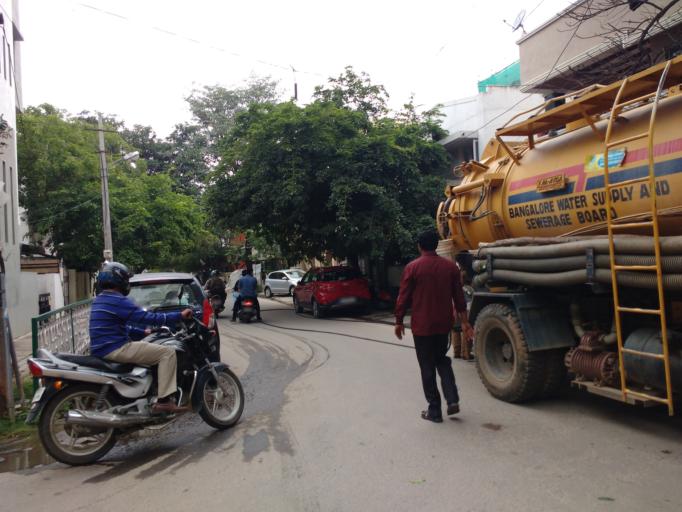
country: IN
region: Karnataka
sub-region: Bangalore Urban
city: Bangalore
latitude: 12.9761
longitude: 77.6357
